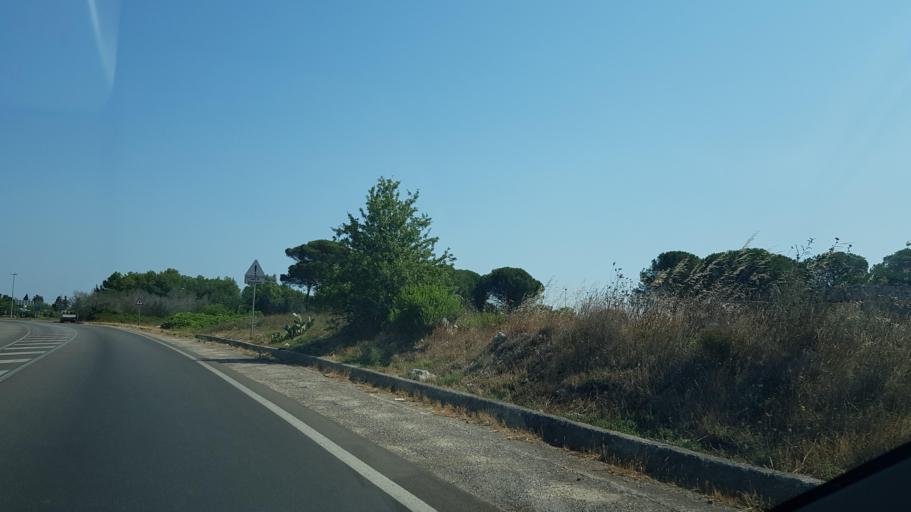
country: IT
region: Apulia
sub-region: Provincia di Lecce
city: Nociglia
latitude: 40.0433
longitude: 18.3225
